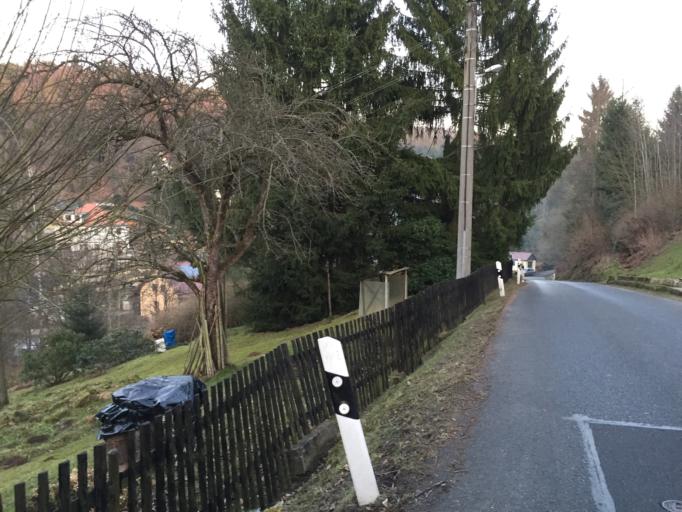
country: DE
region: Saxony
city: Stadt Wehlen
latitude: 50.9540
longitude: 14.0401
